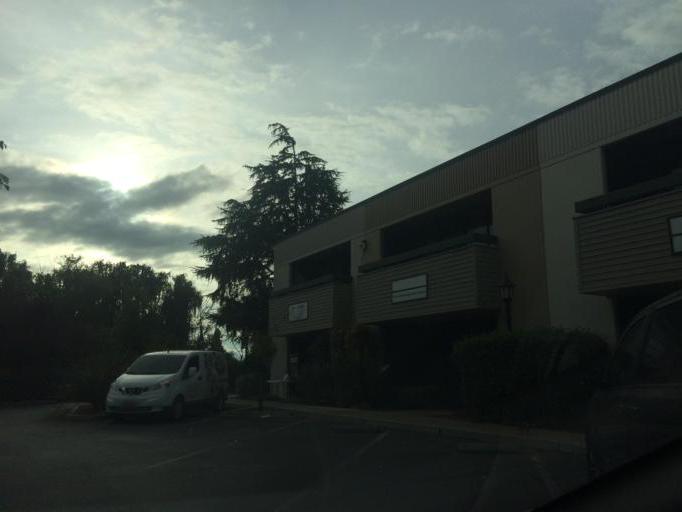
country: US
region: California
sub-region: Santa Clara County
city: Milpitas
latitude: 37.3847
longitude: -121.9070
